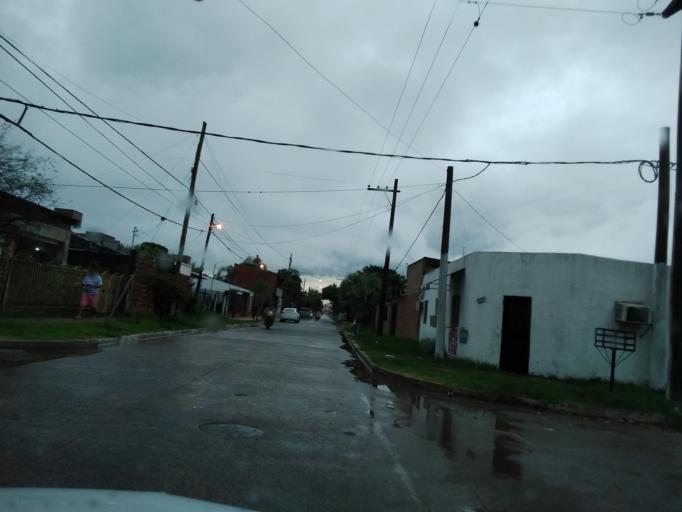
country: AR
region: Corrientes
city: Corrientes
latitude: -27.4943
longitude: -58.8203
